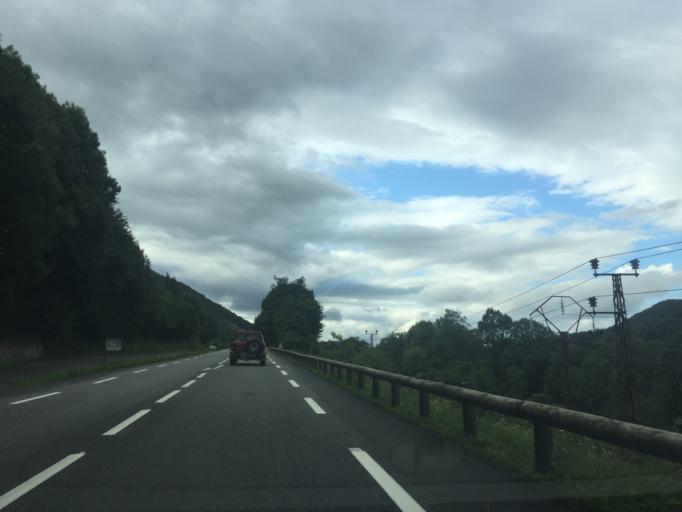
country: FR
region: Midi-Pyrenees
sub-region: Departement des Hautes-Pyrenees
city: La Barthe-de-Neste
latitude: 43.0050
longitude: 0.3783
